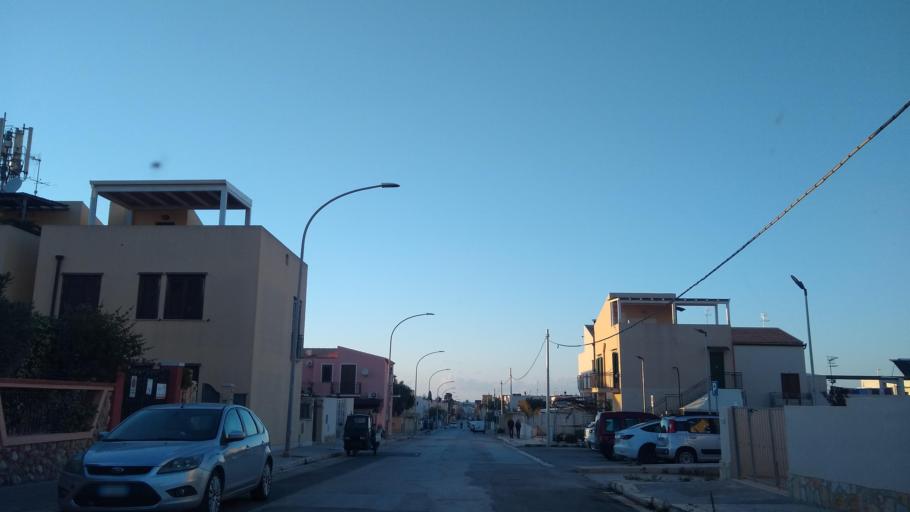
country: IT
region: Sicily
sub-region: Trapani
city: San Vito Lo Capo
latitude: 38.1682
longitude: 12.7360
